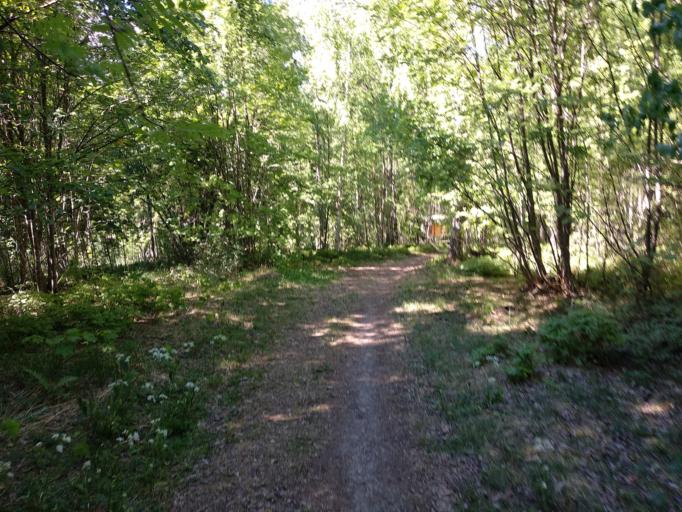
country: FI
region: Pirkanmaa
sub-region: Tampere
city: Kangasala
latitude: 61.4378
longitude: 24.1273
